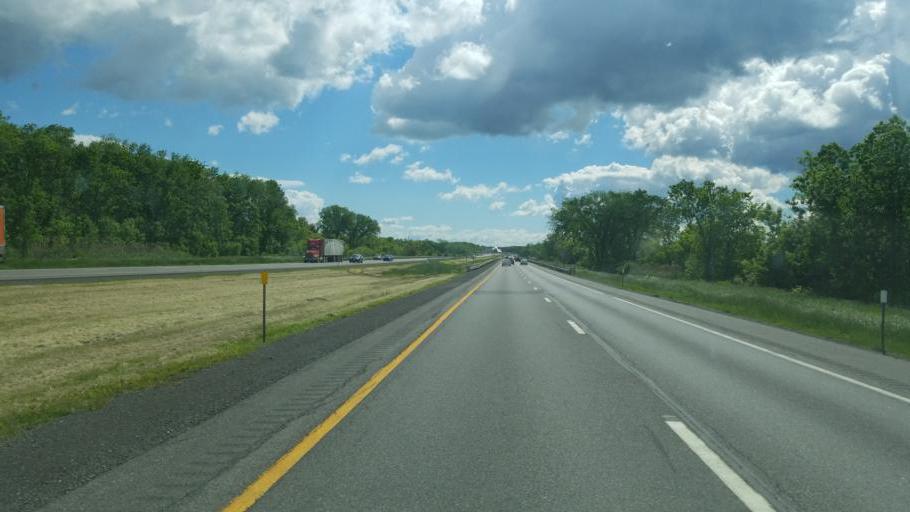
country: US
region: New York
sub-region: Madison County
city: Bolivar
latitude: 43.0954
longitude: -75.8614
